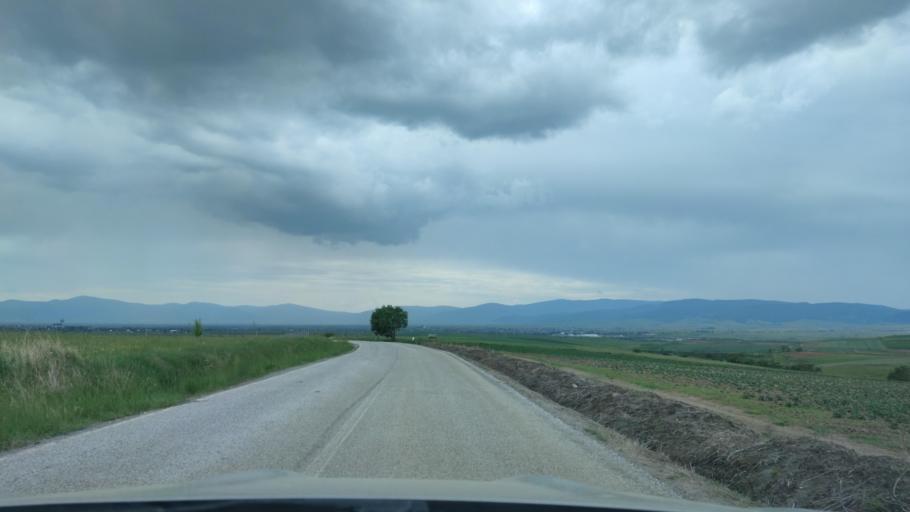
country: RO
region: Harghita
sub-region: Comuna Ditrau
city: Ditrau
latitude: 46.8416
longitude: 25.4979
